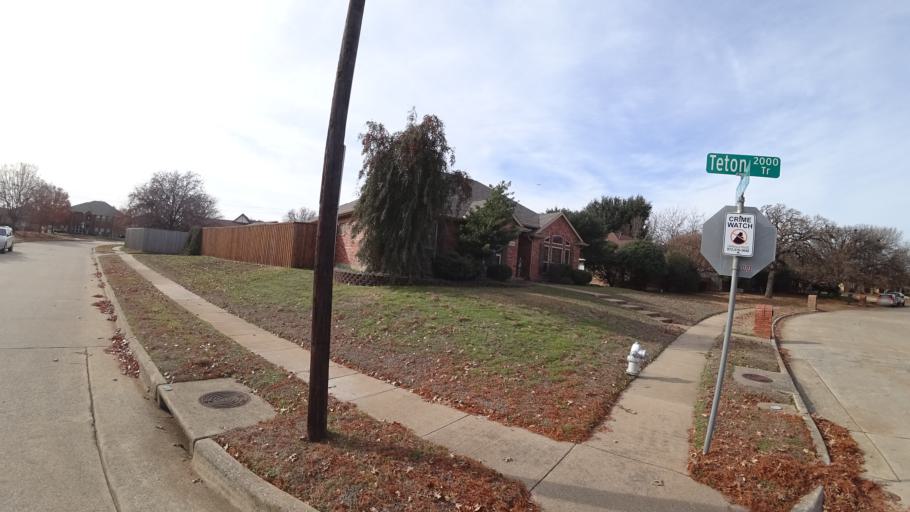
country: US
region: Texas
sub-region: Denton County
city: Highland Village
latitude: 33.0764
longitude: -97.0380
